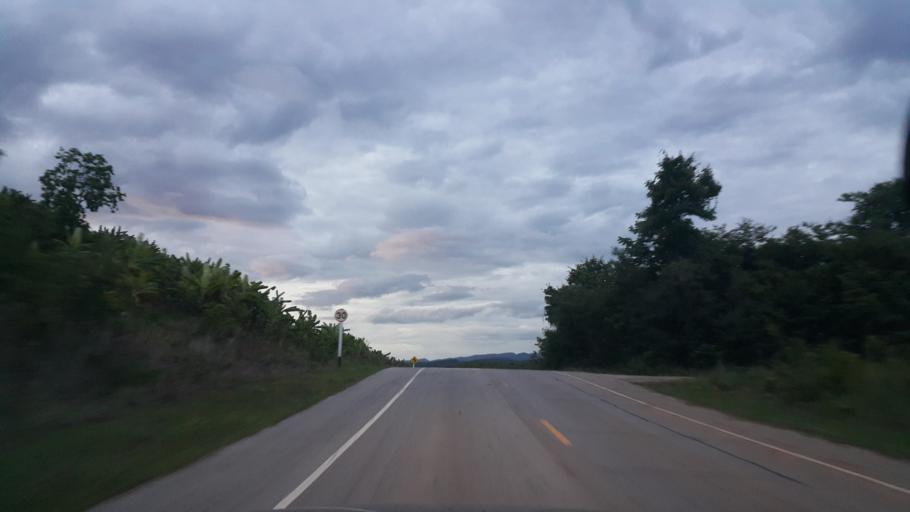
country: TH
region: Loei
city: Phu Ruea
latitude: 17.5220
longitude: 101.2328
